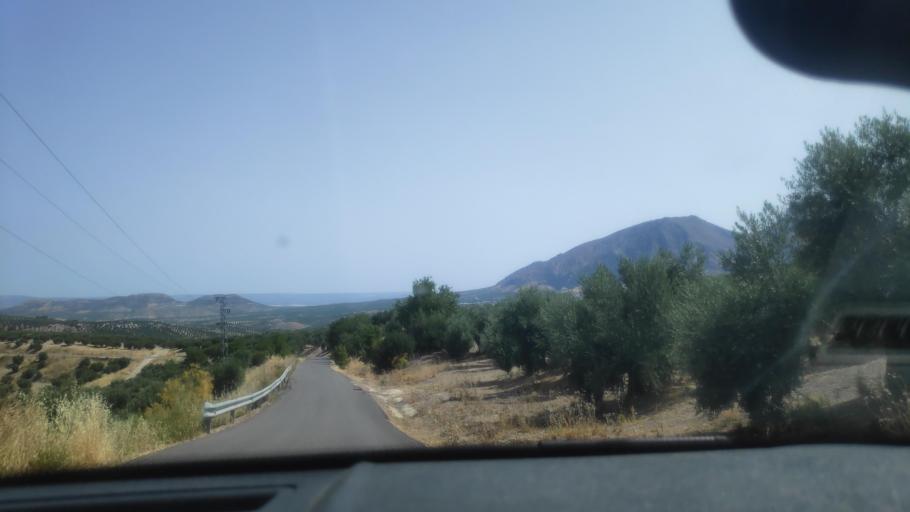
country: ES
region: Andalusia
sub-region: Provincia de Jaen
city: Jimena
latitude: 37.7951
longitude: -3.4490
